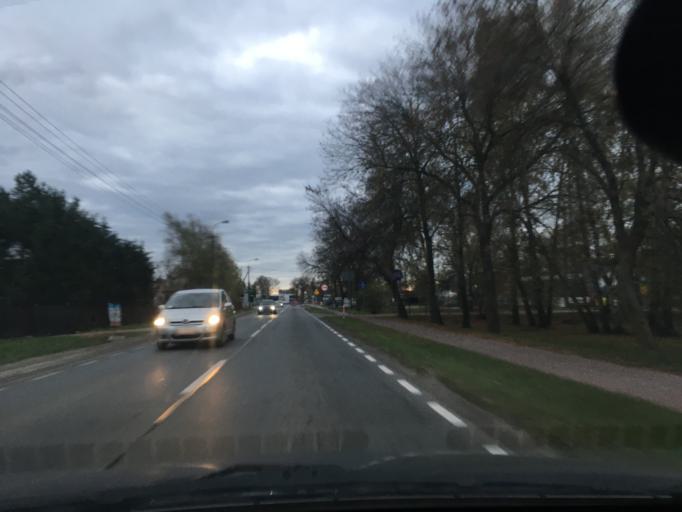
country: PL
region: Masovian Voivodeship
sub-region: Powiat piaseczynski
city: Lesznowola
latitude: 52.0920
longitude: 20.9318
